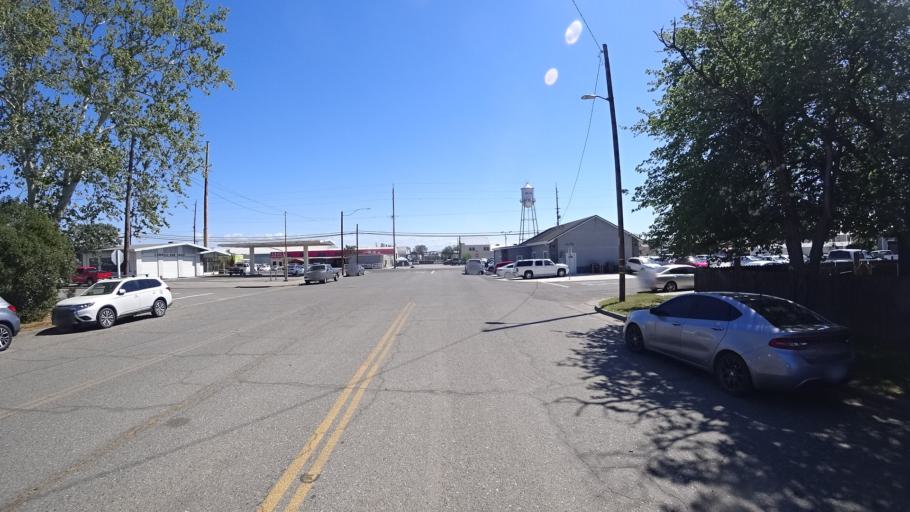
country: US
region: California
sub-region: Glenn County
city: Orland
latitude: 39.7485
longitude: -122.1985
